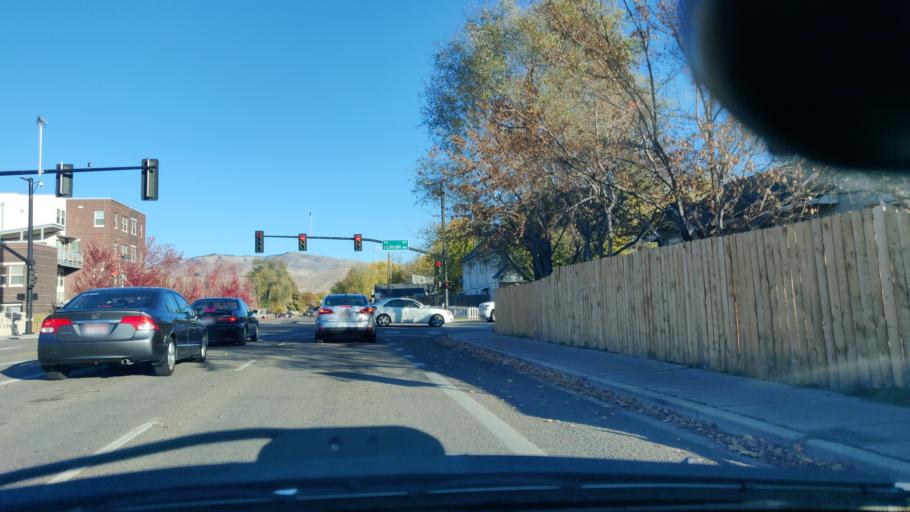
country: US
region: Idaho
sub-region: Ada County
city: Boise
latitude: 43.5983
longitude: -116.2029
